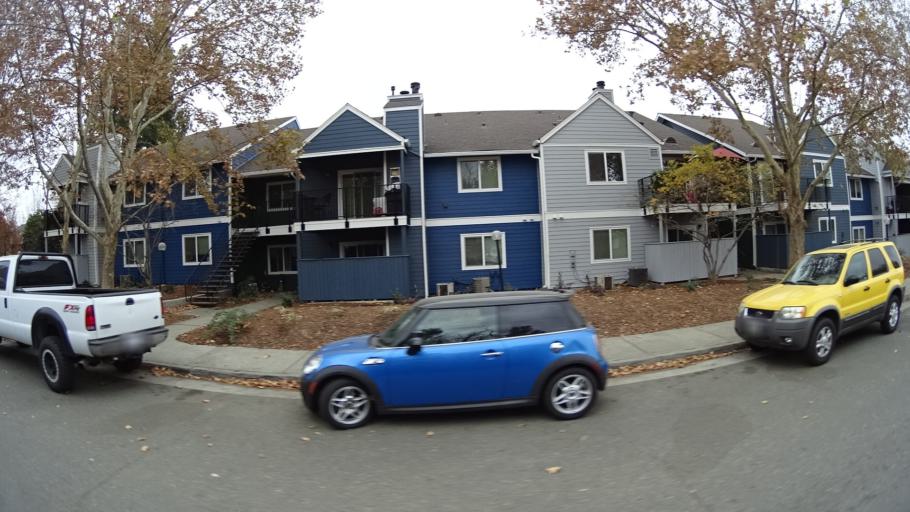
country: US
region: California
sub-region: Sacramento County
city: Citrus Heights
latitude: 38.7011
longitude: -121.2887
